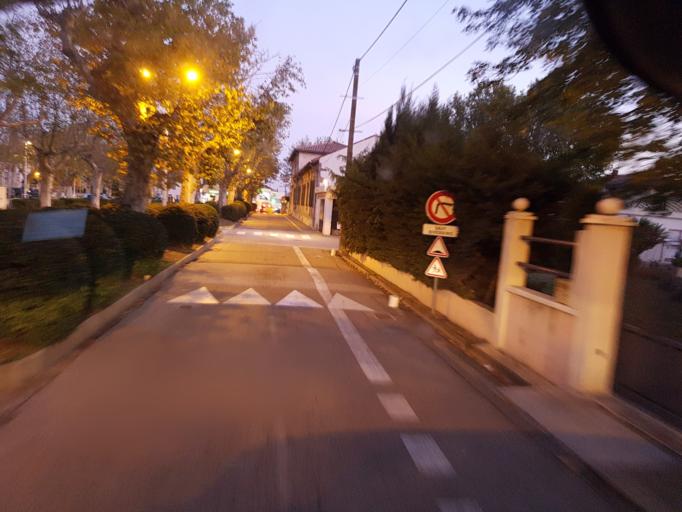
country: FR
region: Languedoc-Roussillon
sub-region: Departement du Gard
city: Bellegarde
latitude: 43.7559
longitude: 4.5141
